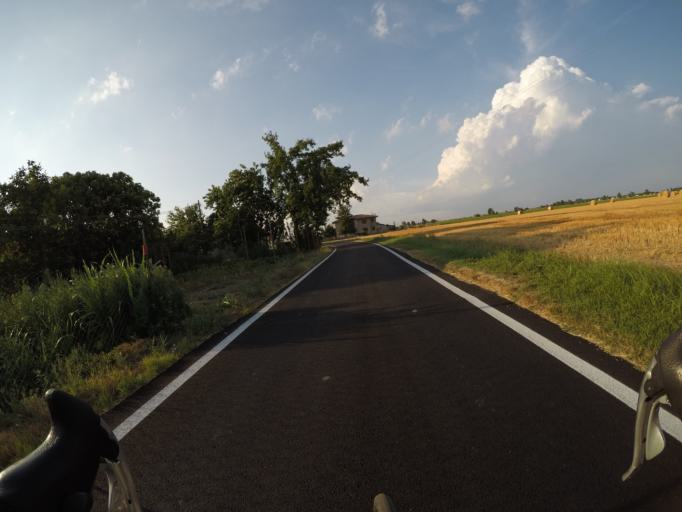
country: IT
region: Veneto
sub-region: Provincia di Rovigo
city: San Bellino
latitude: 45.0378
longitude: 11.5896
